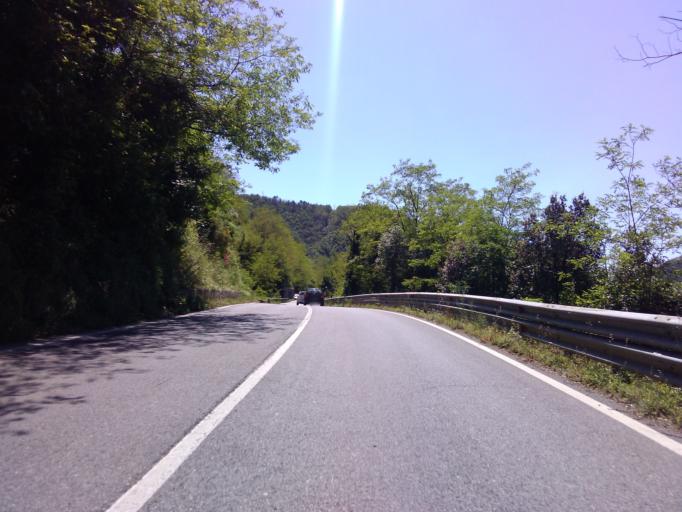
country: IT
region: Tuscany
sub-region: Provincia di Massa-Carrara
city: Podenzana
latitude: 44.1883
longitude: 9.9397
